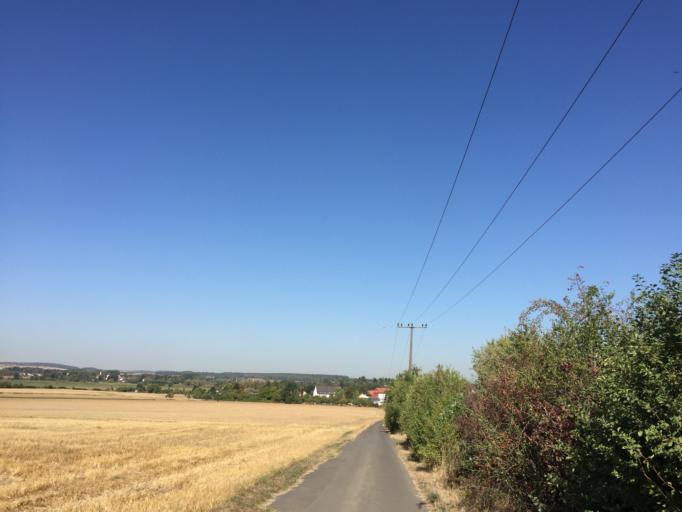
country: DE
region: Hesse
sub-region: Regierungsbezirk Giessen
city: Hungen
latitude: 50.4367
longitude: 8.9283
